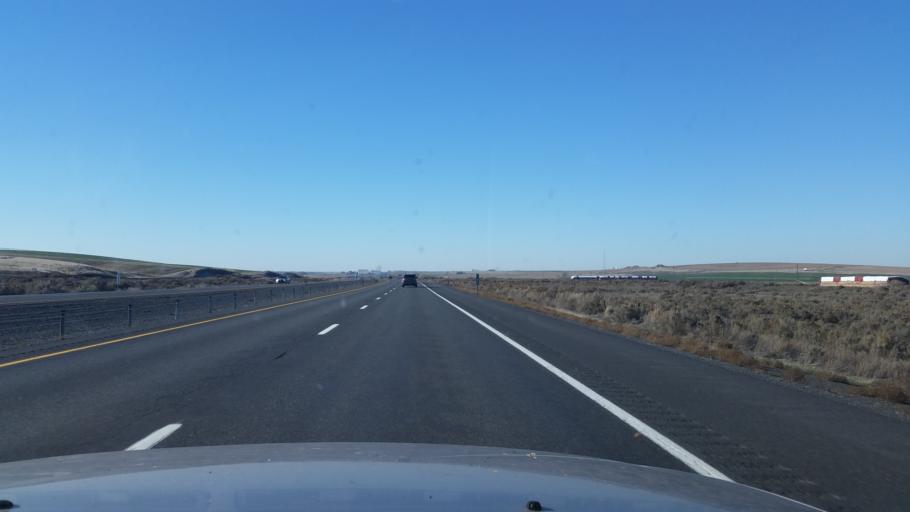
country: US
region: Washington
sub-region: Grant County
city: Warden
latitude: 47.0851
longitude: -118.9983
